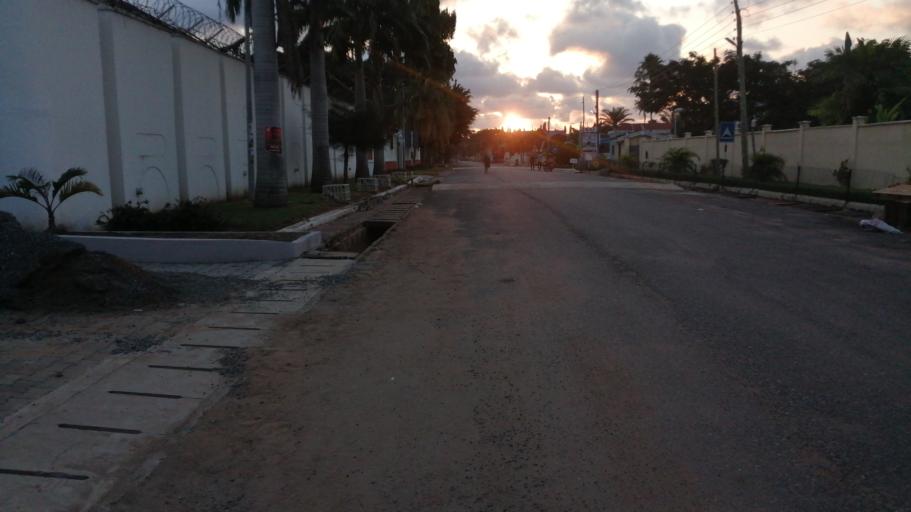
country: GH
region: Greater Accra
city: Medina Estates
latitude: 5.6189
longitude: -0.1803
